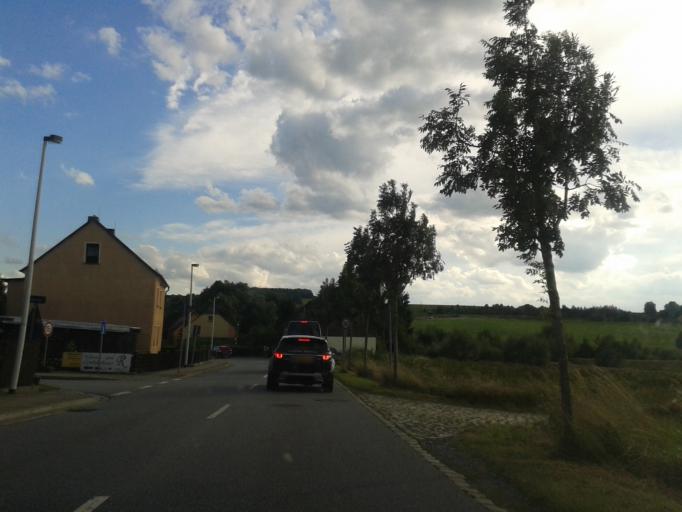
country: DE
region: Saxony
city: Durrrohrsdorf
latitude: 51.0444
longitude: 13.9342
